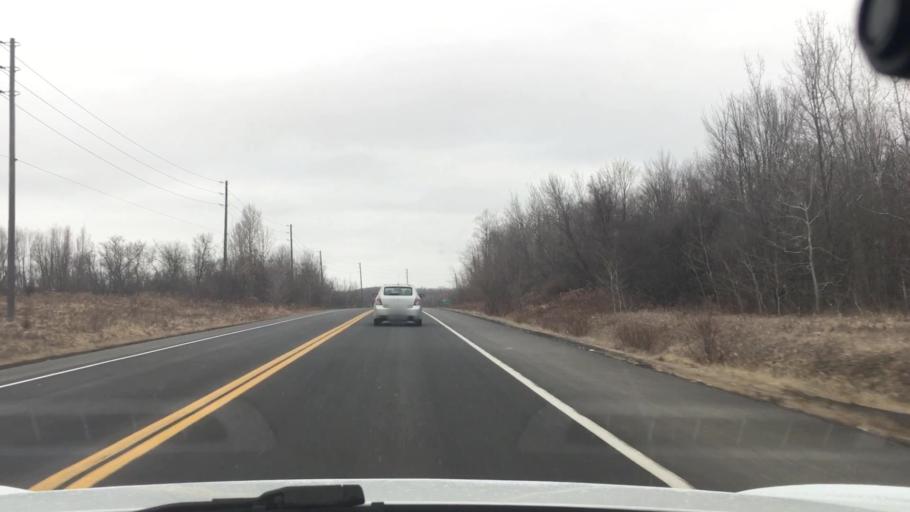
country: CA
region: Ontario
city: Pickering
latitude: 43.8938
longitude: -79.1938
